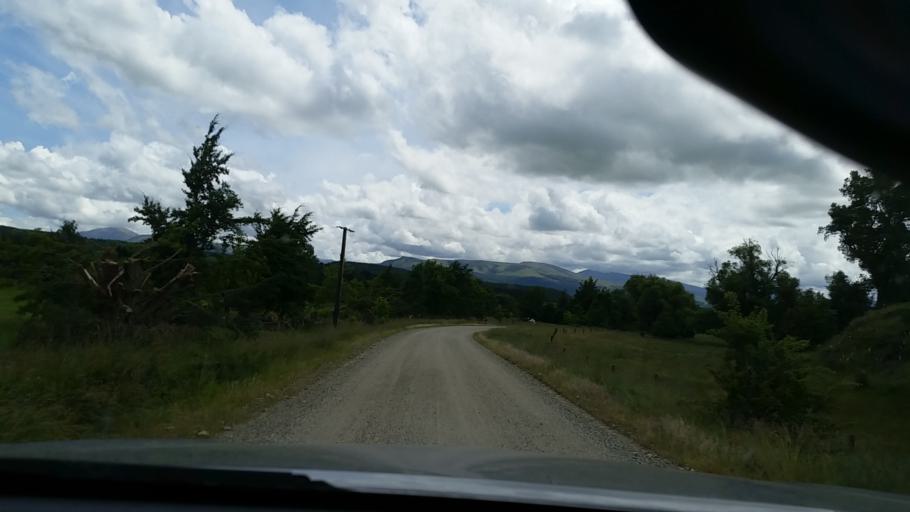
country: NZ
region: Southland
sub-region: Gore District
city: Gore
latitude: -45.7243
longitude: 168.8577
